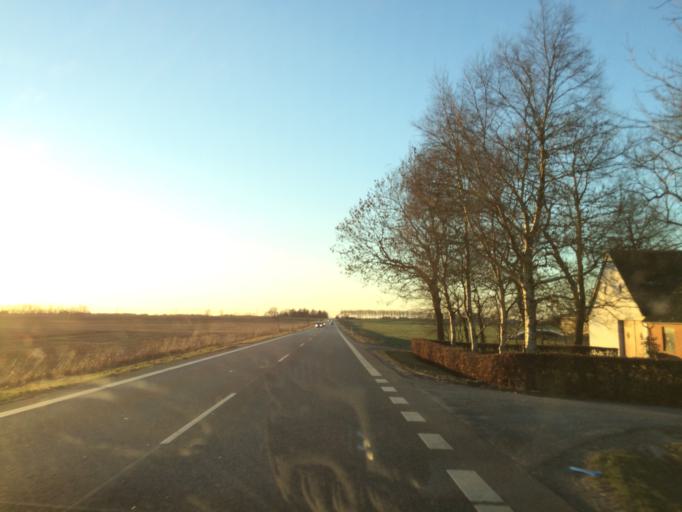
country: DK
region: Central Jutland
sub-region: Viborg Kommune
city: Bjerringbro
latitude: 56.4788
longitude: 9.5986
